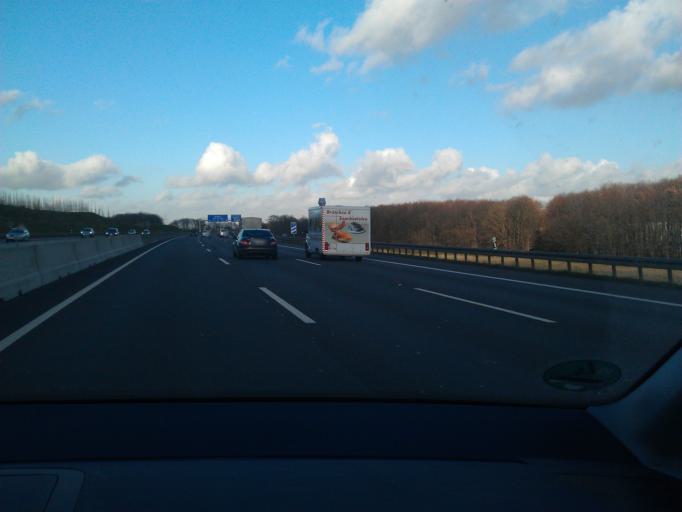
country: DE
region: North Rhine-Westphalia
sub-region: Regierungsbezirk Koln
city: Mengenich
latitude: 50.9705
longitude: 6.8502
